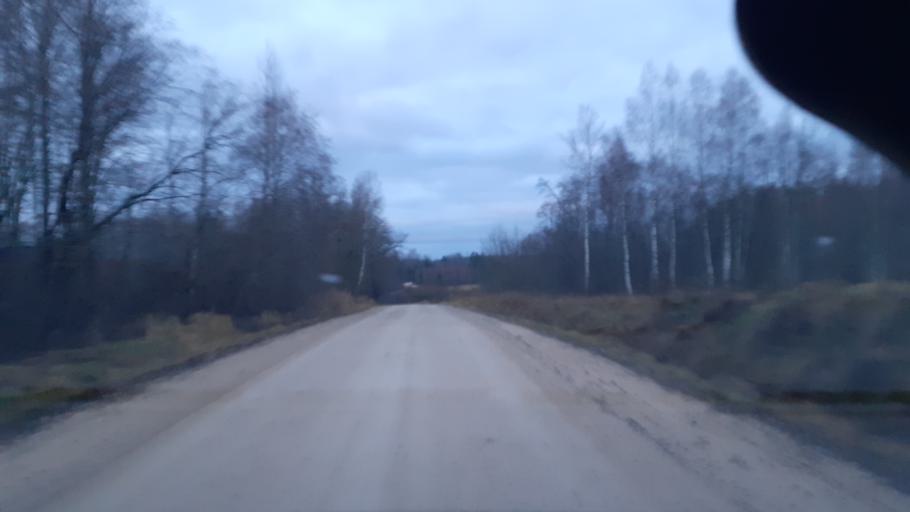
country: LV
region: Kuldigas Rajons
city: Kuldiga
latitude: 56.9559
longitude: 21.8006
